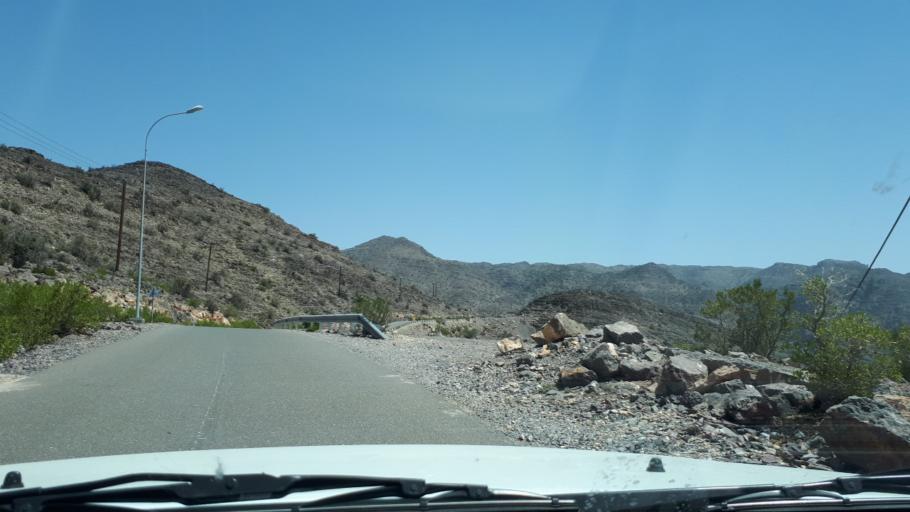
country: OM
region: Muhafazat ad Dakhiliyah
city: Izki
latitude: 23.0851
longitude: 57.7233
